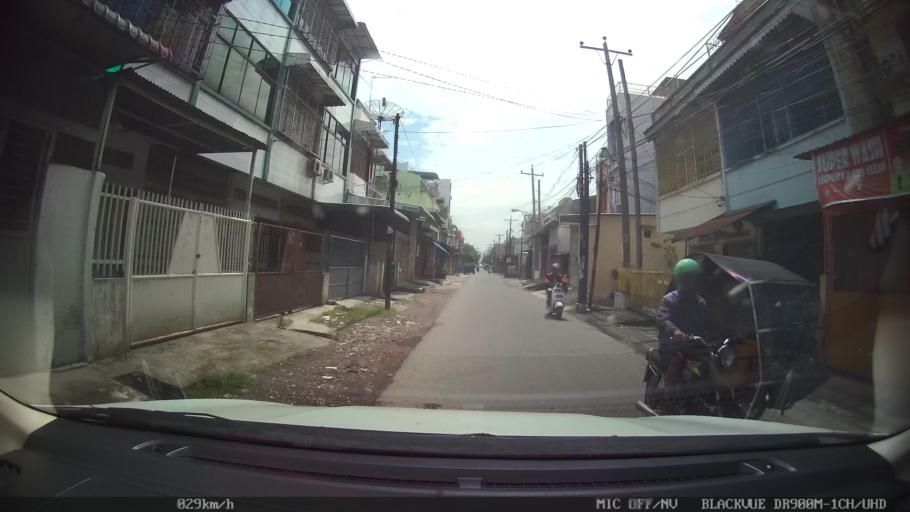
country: ID
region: North Sumatra
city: Medan
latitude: 3.5874
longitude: 98.7089
